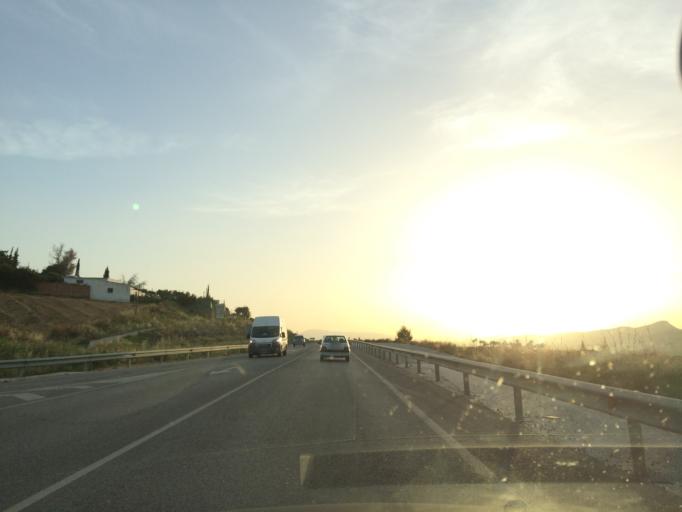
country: ES
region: Andalusia
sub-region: Provincia de Malaga
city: Alhaurin de la Torre
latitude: 36.6695
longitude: -4.5672
